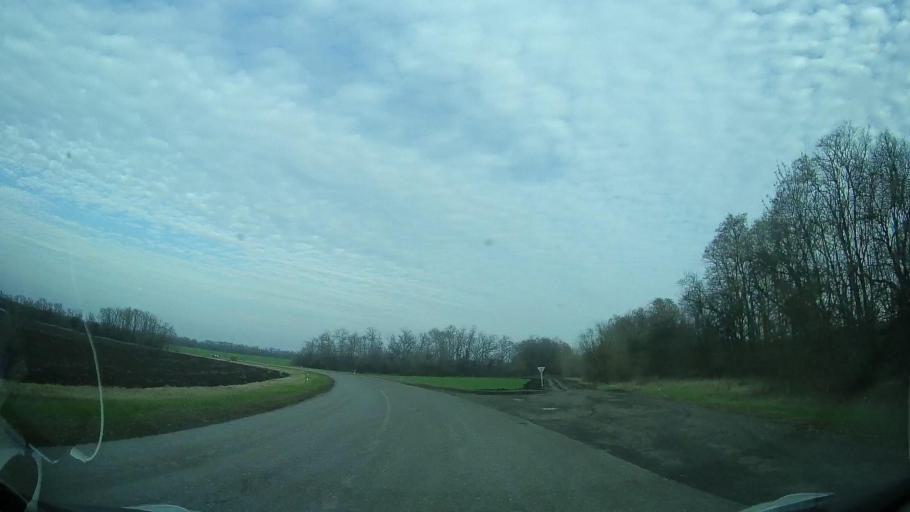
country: RU
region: Rostov
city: Zernograd
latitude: 46.9656
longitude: 40.3887
